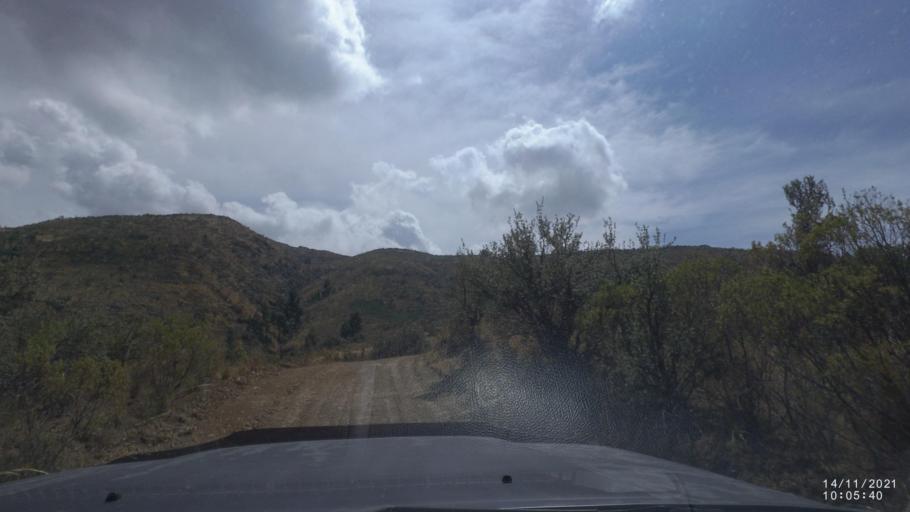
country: BO
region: Cochabamba
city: Cochabamba
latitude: -17.3484
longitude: -66.0912
